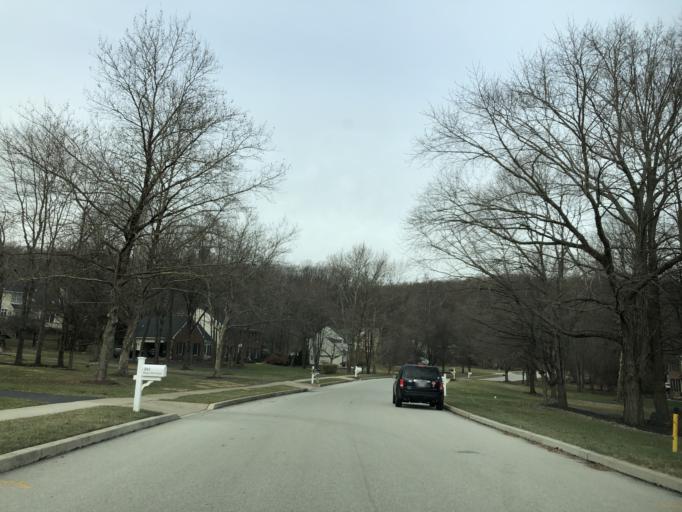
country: US
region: Pennsylvania
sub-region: Chester County
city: Exton
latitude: 40.0354
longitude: -75.6461
